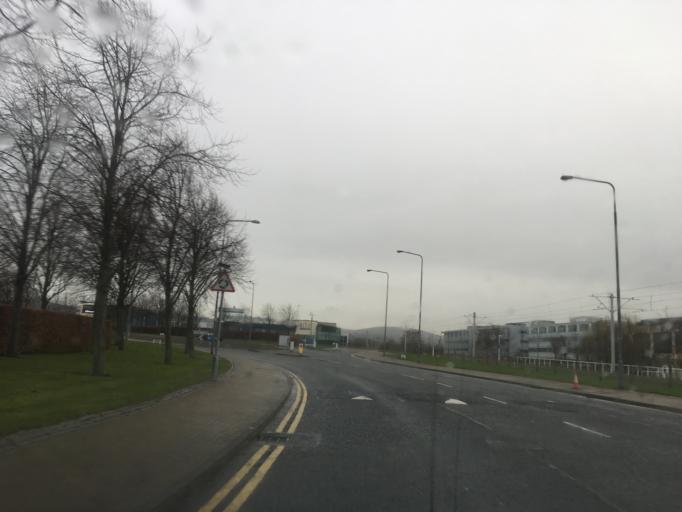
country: GB
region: Scotland
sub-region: Edinburgh
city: Currie
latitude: 55.9344
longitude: -3.3159
